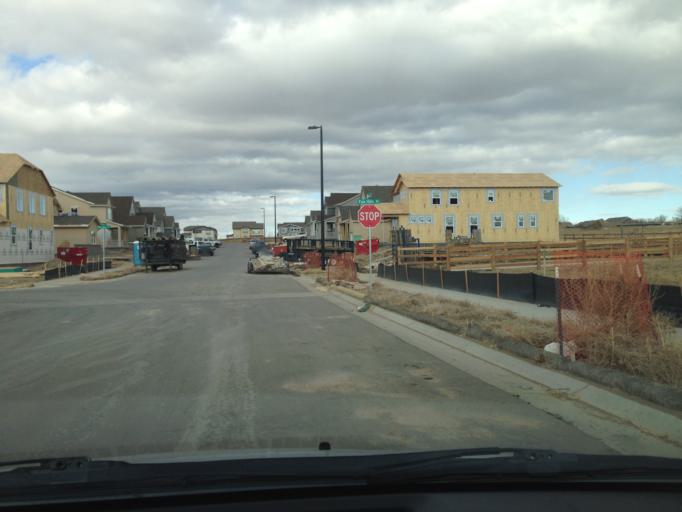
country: US
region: Colorado
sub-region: Boulder County
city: Lafayette
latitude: 40.0274
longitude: -105.0843
